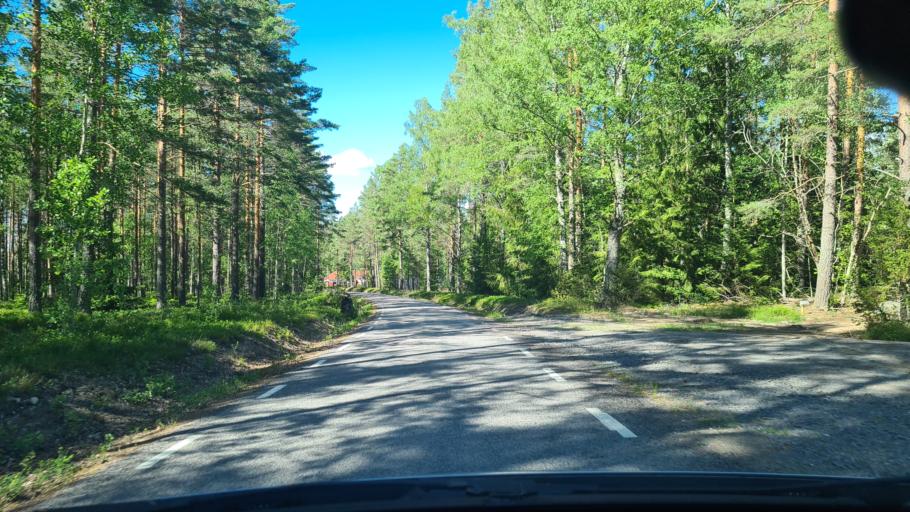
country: SE
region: OEstergoetland
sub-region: Norrkopings Kommun
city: Krokek
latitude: 58.7131
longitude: 16.4290
